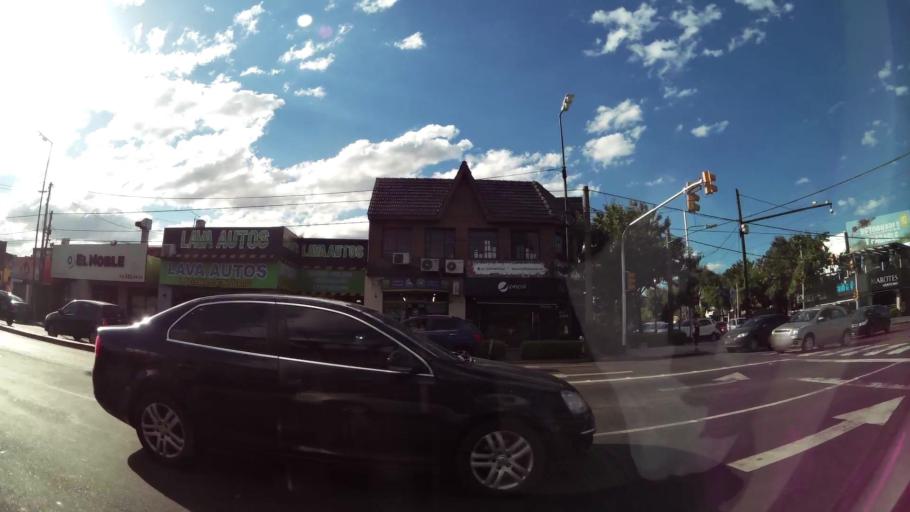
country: AR
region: Buenos Aires
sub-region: Partido de San Isidro
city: San Isidro
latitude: -34.4924
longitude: -58.5473
